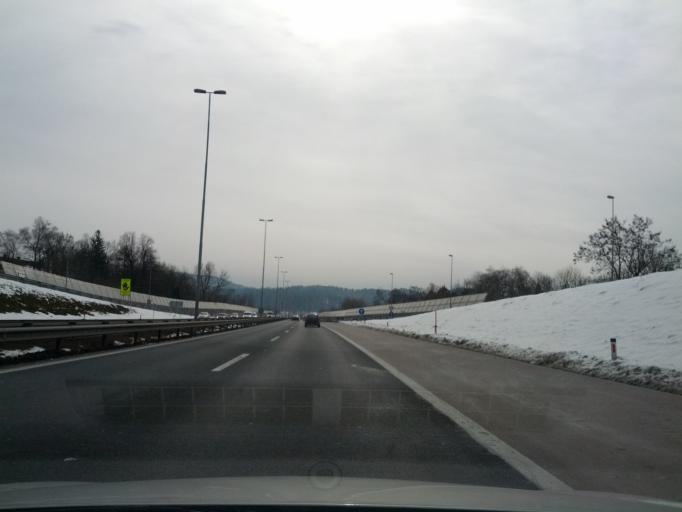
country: SI
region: Dol pri Ljubljani
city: Dol pri Ljubljani
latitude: 46.0542
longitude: 14.5738
